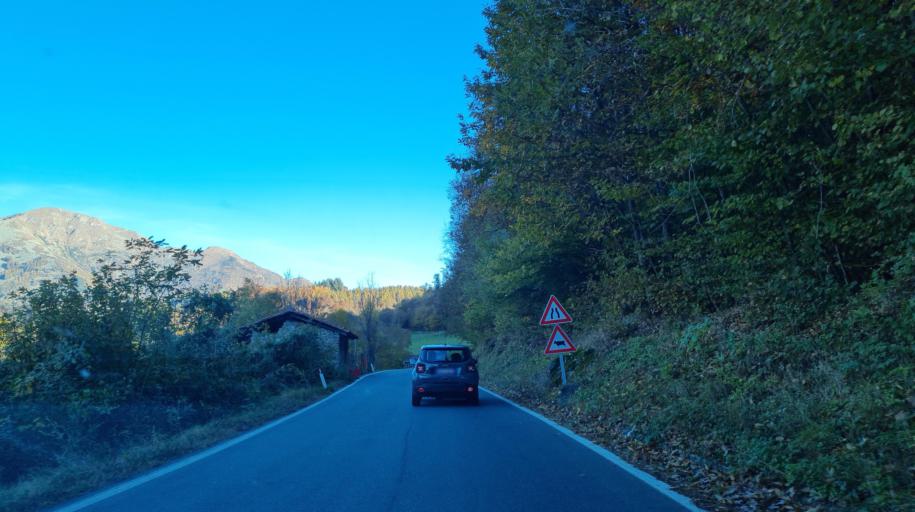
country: IT
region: Piedmont
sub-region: Provincia di Torino
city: Alice Superiore
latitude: 45.4653
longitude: 7.7808
